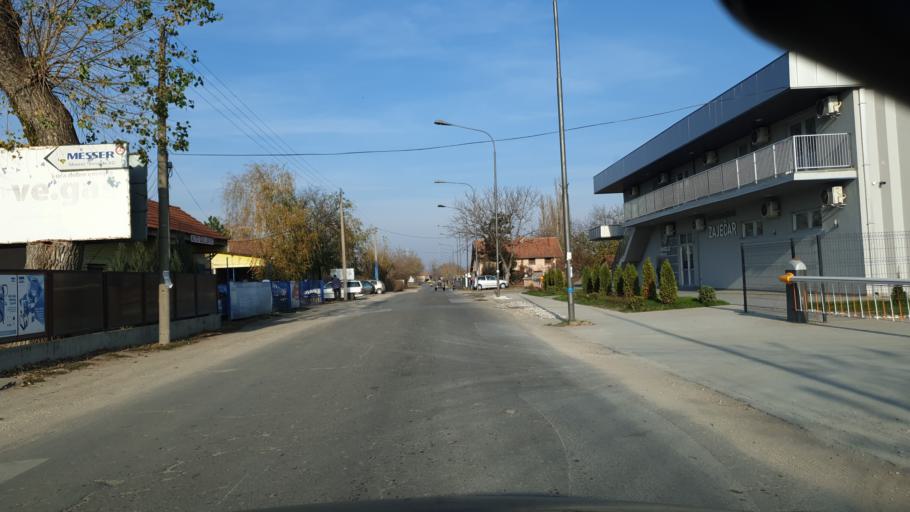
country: RS
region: Central Serbia
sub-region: Zajecarski Okrug
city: Zajecar
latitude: 43.9091
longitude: 22.2890
